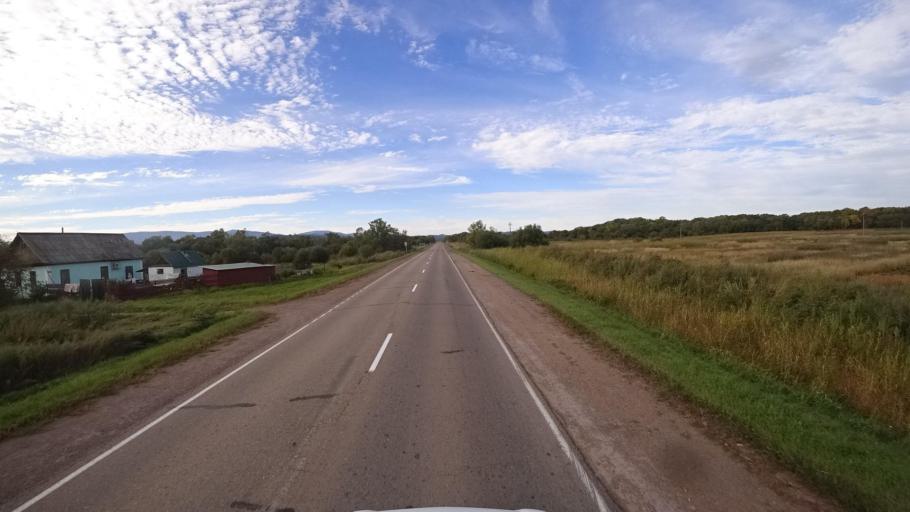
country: RU
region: Primorskiy
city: Dostoyevka
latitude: 44.2991
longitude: 133.4262
